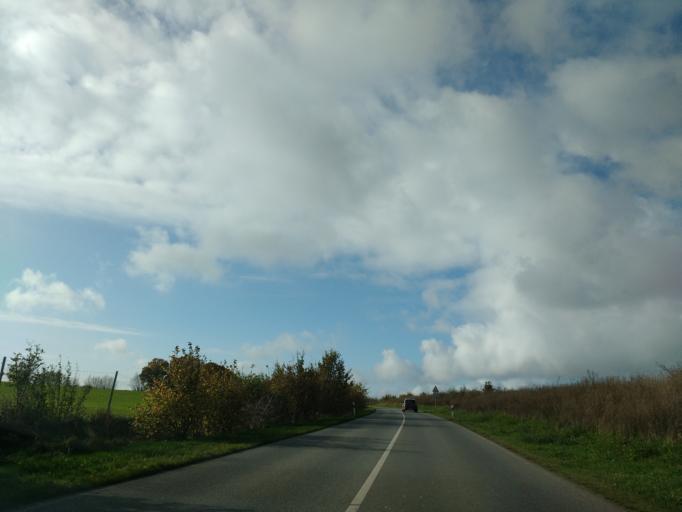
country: DE
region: Mecklenburg-Vorpommern
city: Ostseebad Boltenhagen
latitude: 53.9705
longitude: 11.2379
